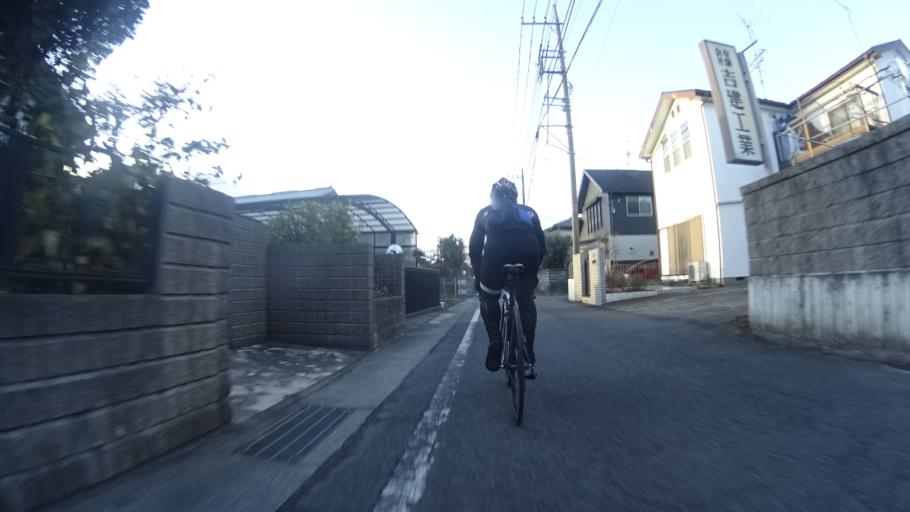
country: JP
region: Kanagawa
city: Atsugi
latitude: 35.4614
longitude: 139.3682
